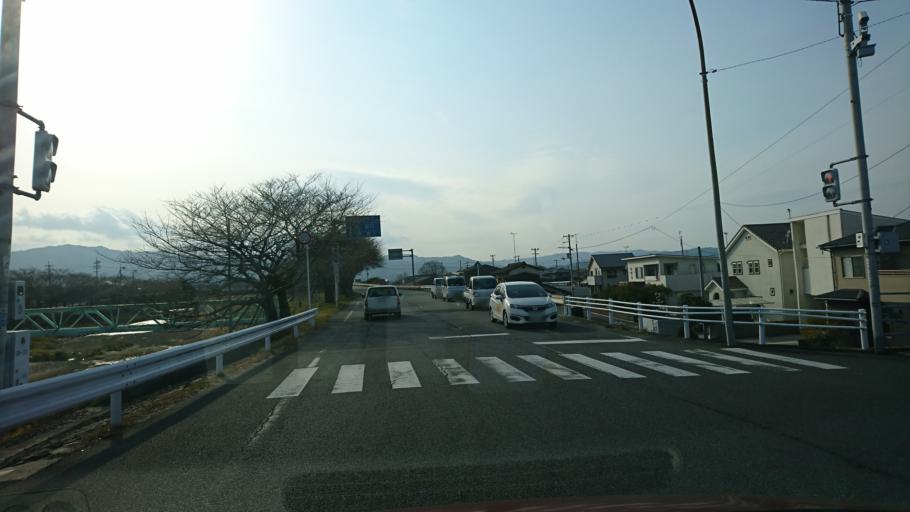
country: JP
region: Ehime
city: Saijo
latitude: 34.0364
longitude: 133.0233
